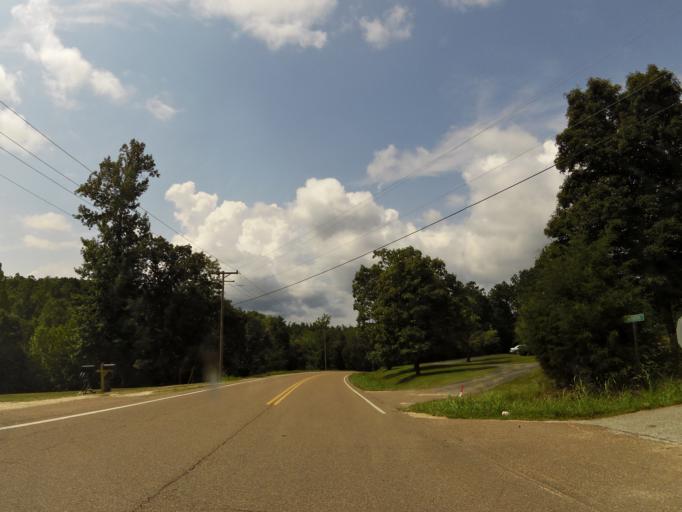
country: US
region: Tennessee
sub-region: Perry County
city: Linden
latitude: 35.6235
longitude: -87.8699
